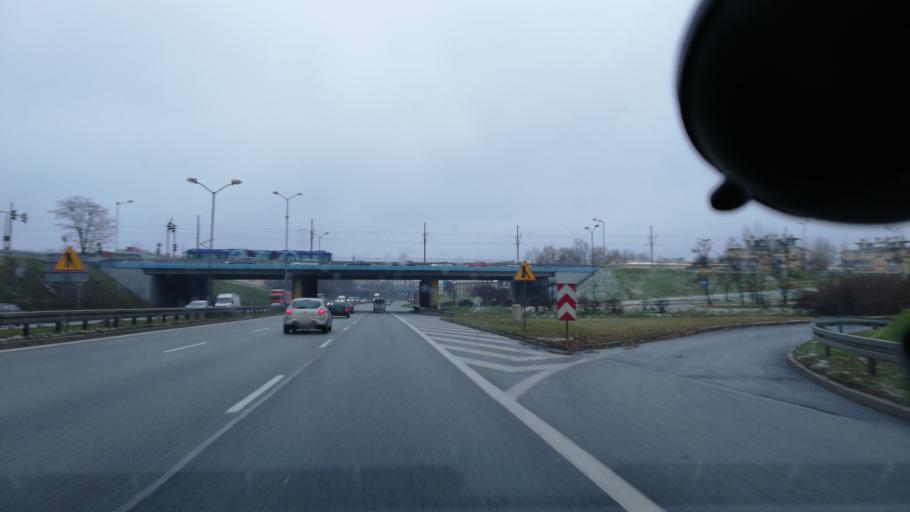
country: PL
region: Silesian Voivodeship
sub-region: Swietochlowice
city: Swietochlowice
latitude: 50.2828
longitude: 18.9472
